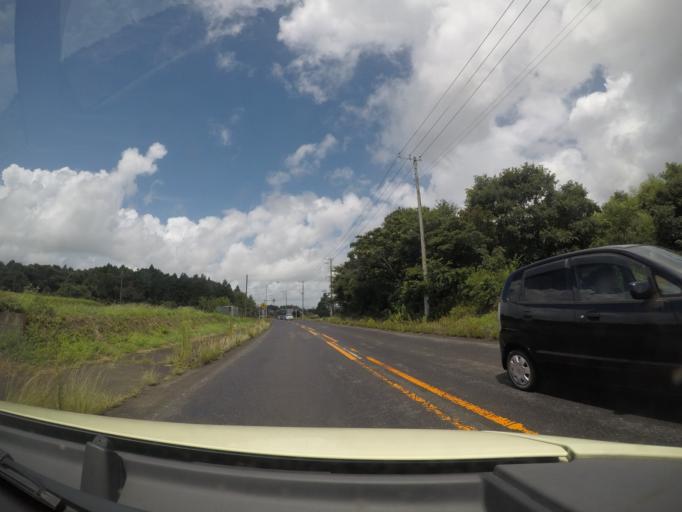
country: JP
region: Ibaraki
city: Ishige
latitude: 36.0803
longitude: 140.0171
